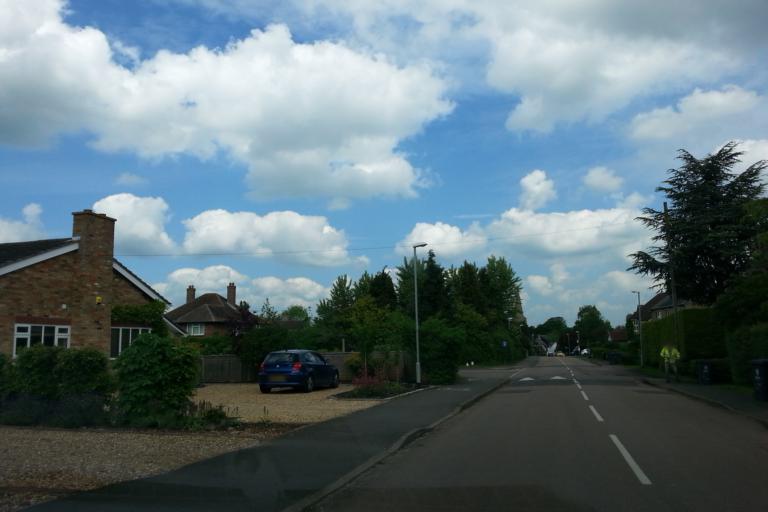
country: GB
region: England
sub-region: Cambridgeshire
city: Swavesey
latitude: 52.3146
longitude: 0.0085
